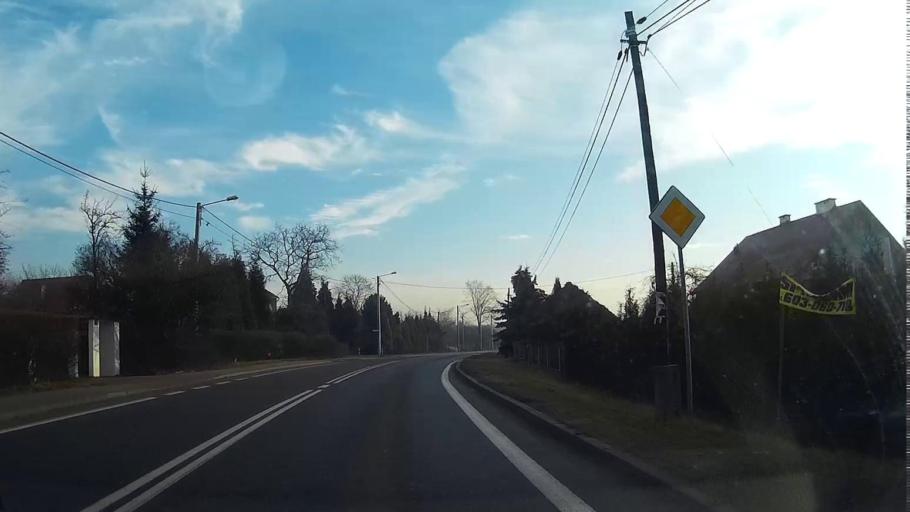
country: PL
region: Lesser Poland Voivodeship
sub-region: Powiat chrzanowski
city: Babice
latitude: 50.0704
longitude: 19.4563
